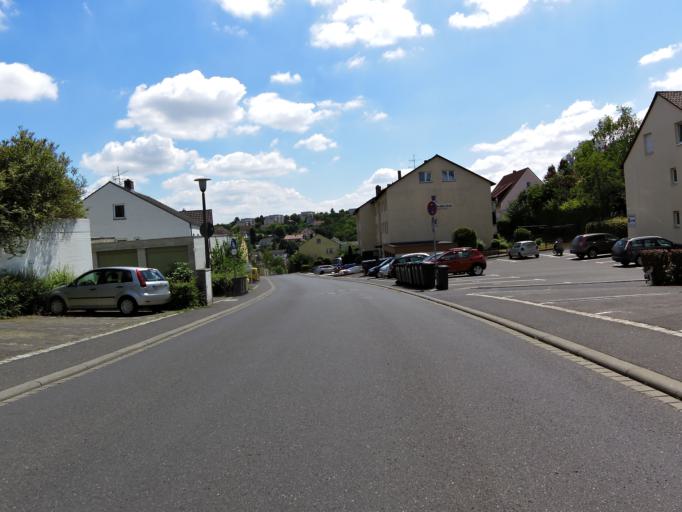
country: DE
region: Bavaria
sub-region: Regierungsbezirk Unterfranken
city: Gerbrunn
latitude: 49.7806
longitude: 9.9871
